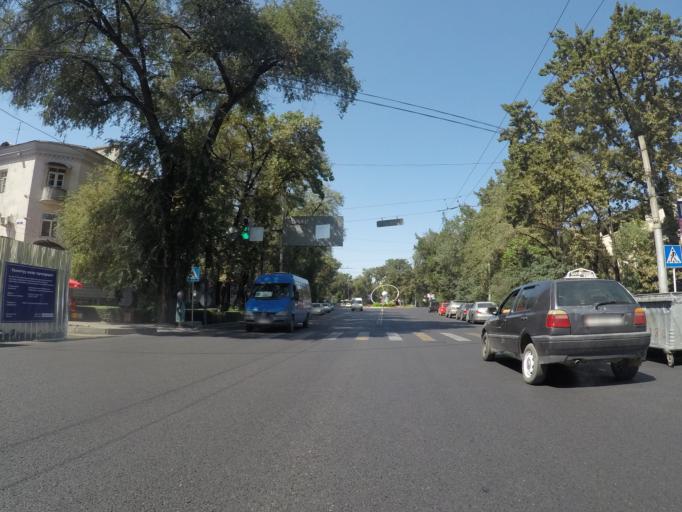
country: KG
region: Chuy
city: Bishkek
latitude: 42.8769
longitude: 74.5815
